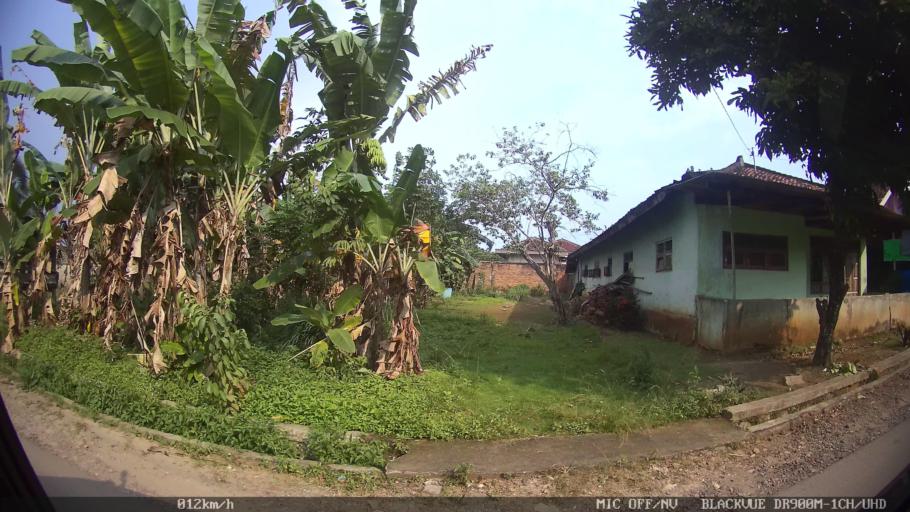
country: ID
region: Lampung
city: Kedaton
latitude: -5.3549
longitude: 105.2222
